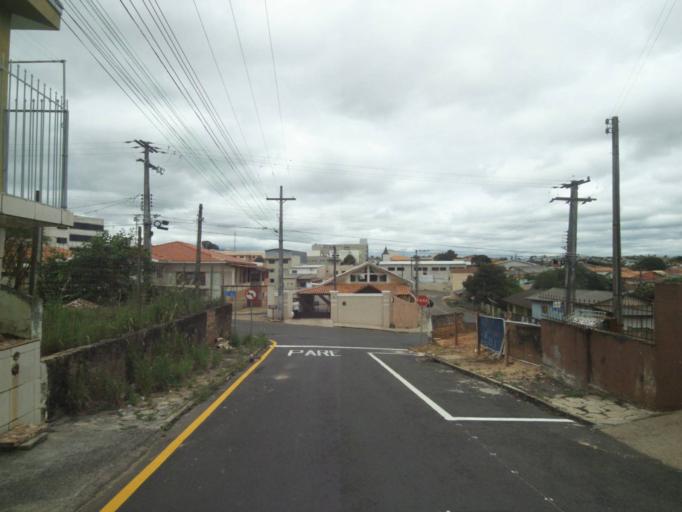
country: BR
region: Parana
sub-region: Telemaco Borba
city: Telemaco Borba
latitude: -24.3217
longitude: -50.6200
